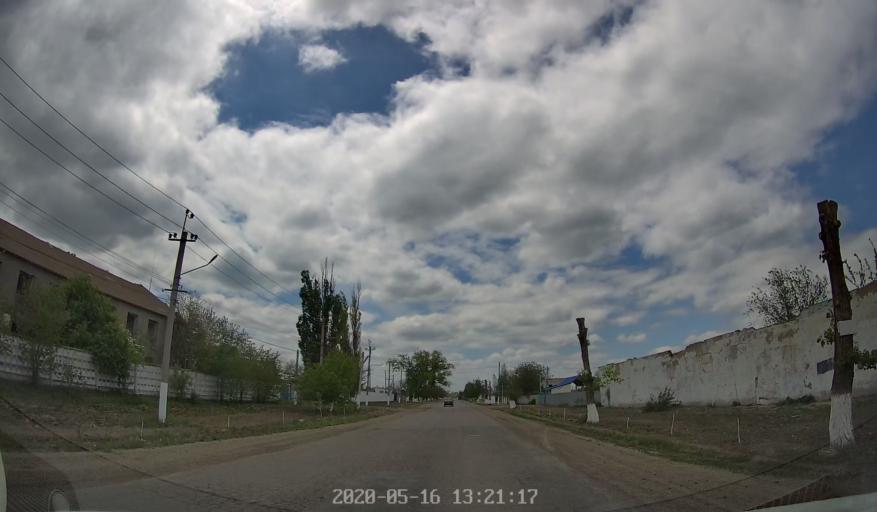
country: UA
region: Odessa
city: Lymanske
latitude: 46.5409
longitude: 30.0375
